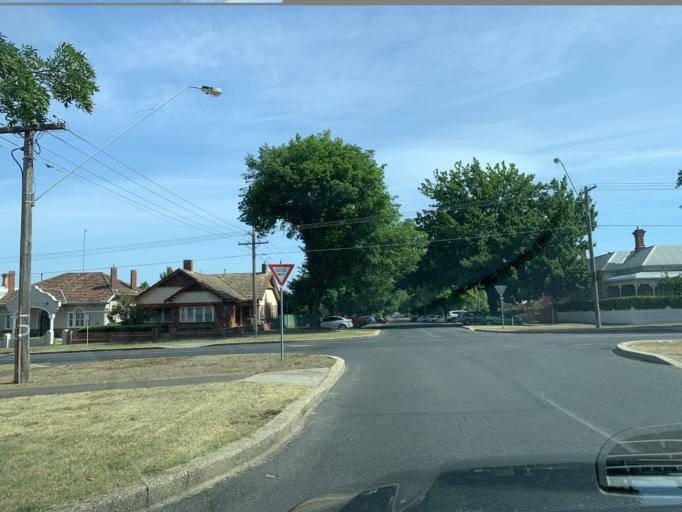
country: AU
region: Victoria
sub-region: Ballarat North
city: Ballarat Central
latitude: -37.5632
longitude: 143.8515
